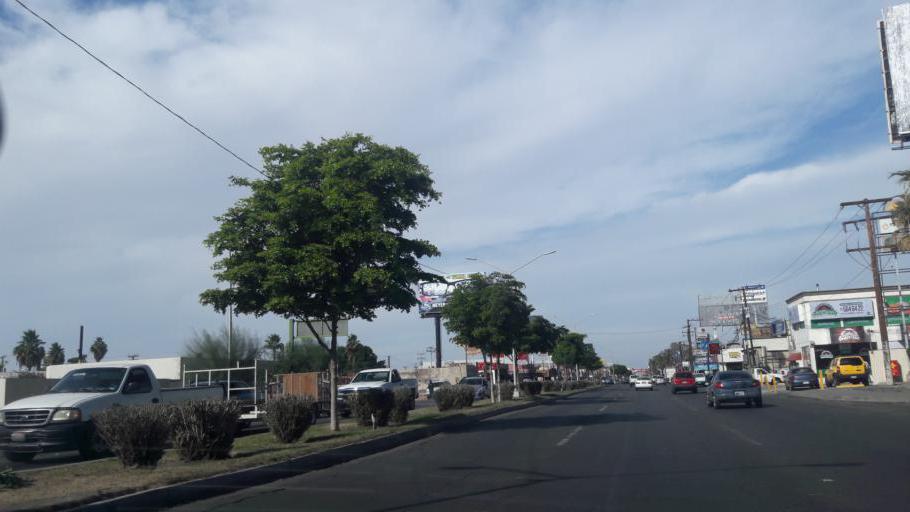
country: MX
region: Baja California
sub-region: Mexicali
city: Mexicali
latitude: 32.6261
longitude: -115.4442
